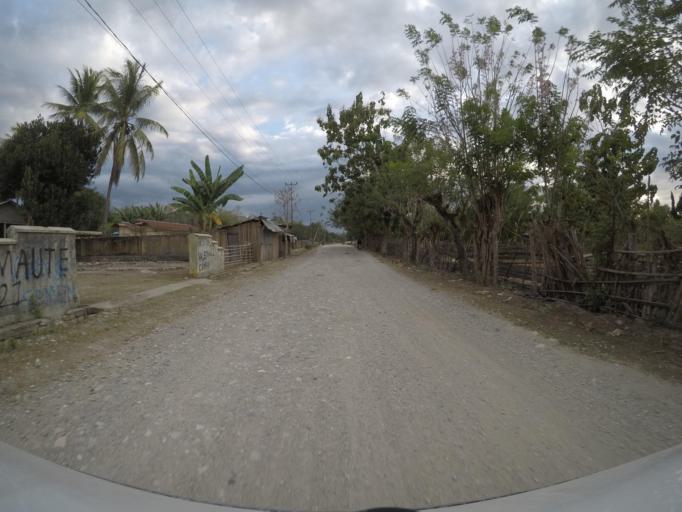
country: TL
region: Bobonaro
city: Maliana
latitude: -8.8794
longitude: 125.2118
